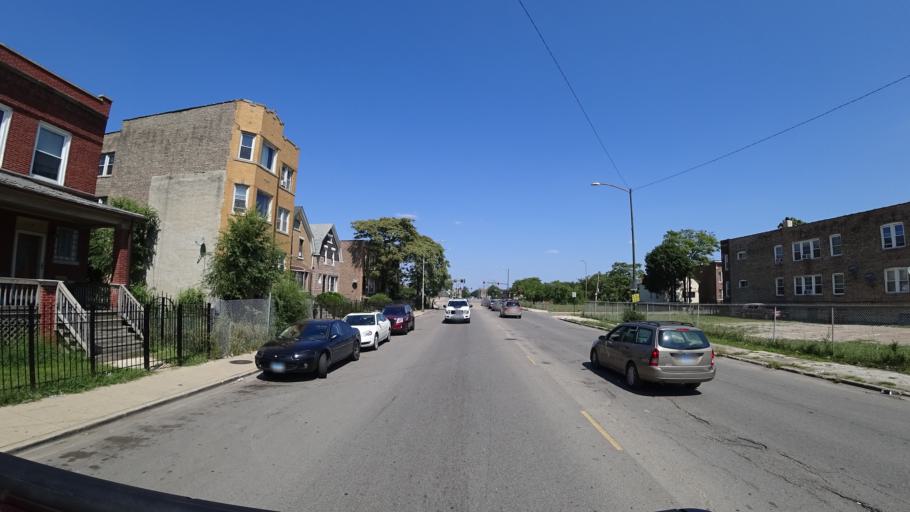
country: US
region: Illinois
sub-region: Cook County
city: Cicero
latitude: 41.8720
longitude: -87.7352
